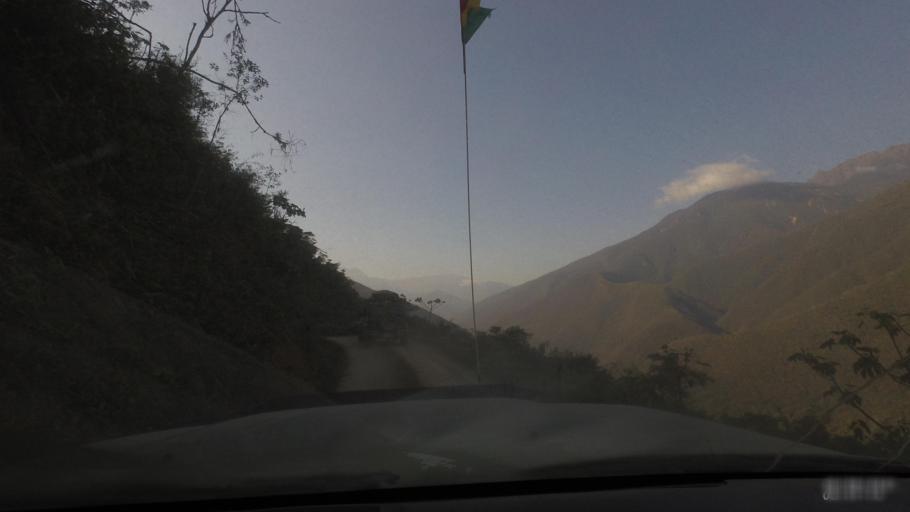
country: BO
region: La Paz
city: Quime
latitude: -16.5208
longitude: -66.7706
